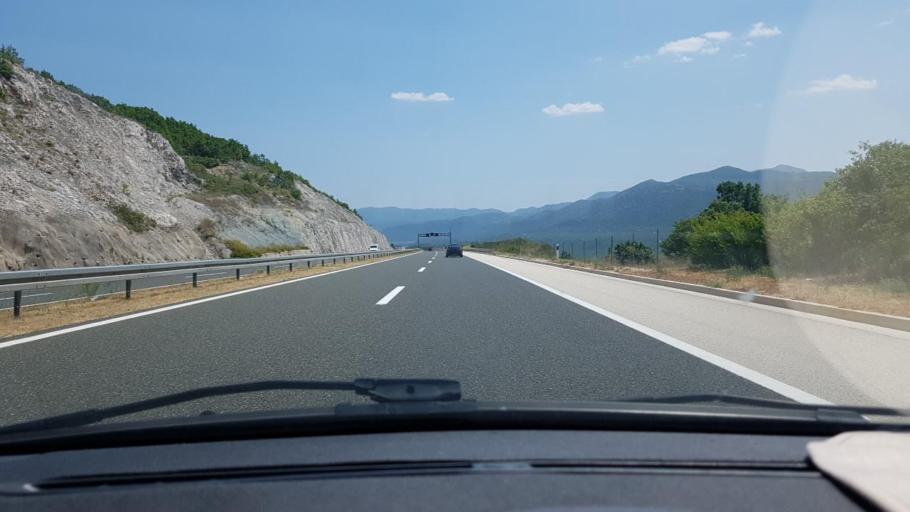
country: HR
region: Splitsko-Dalmatinska
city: Runovic
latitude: 43.2968
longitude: 17.1942
